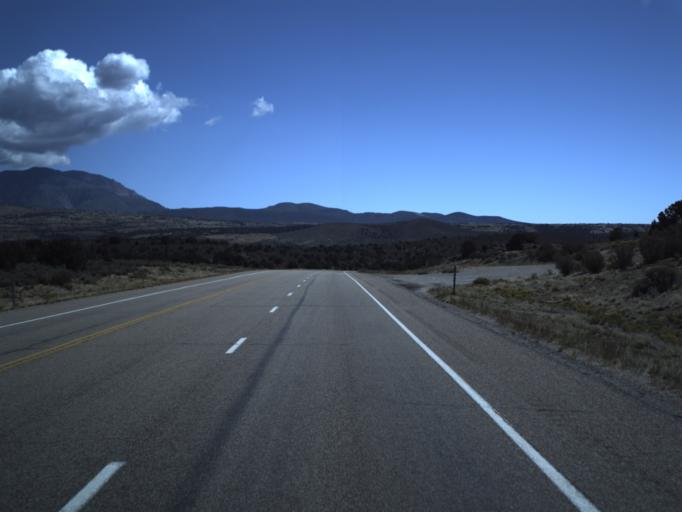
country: US
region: Utah
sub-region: Washington County
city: Ivins
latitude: 37.3197
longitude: -113.6853
